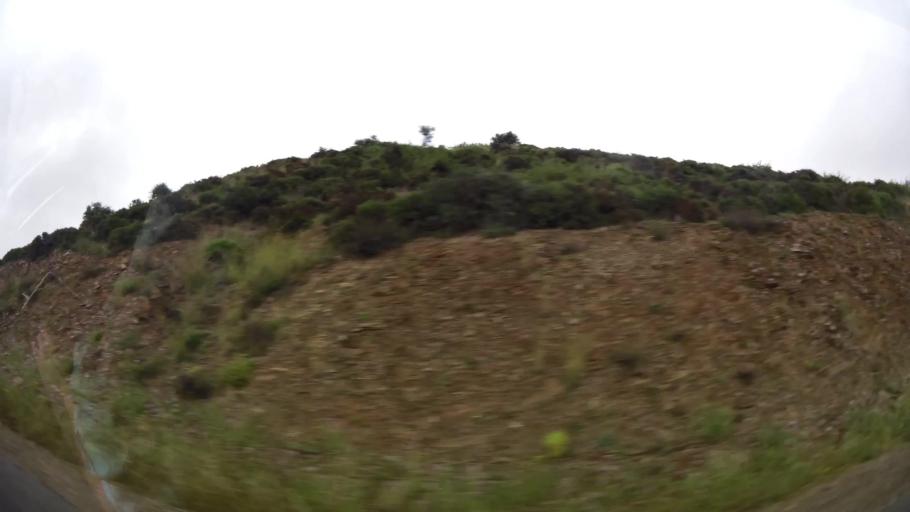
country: MA
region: Oriental
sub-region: Nador
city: Midar
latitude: 35.0683
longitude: -3.4806
